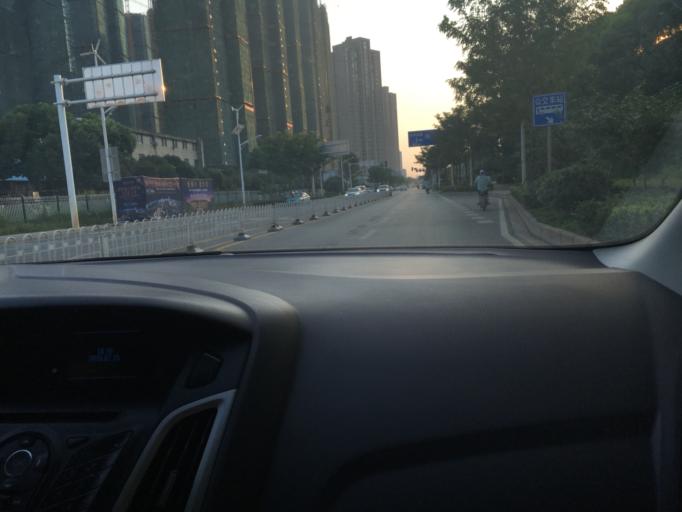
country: CN
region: Hubei
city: Guanshan
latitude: 30.4582
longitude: 114.3826
